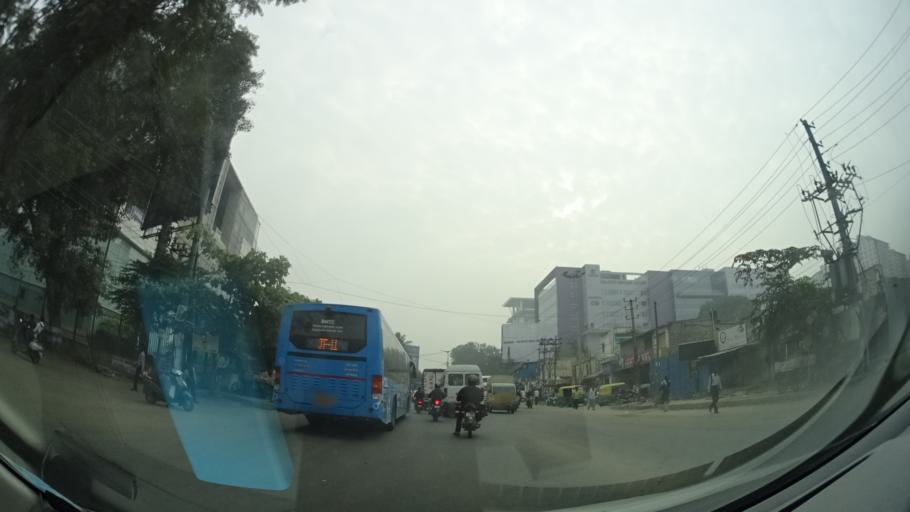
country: IN
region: Karnataka
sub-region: Bangalore Urban
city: Bangalore
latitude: 12.9942
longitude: 77.7011
